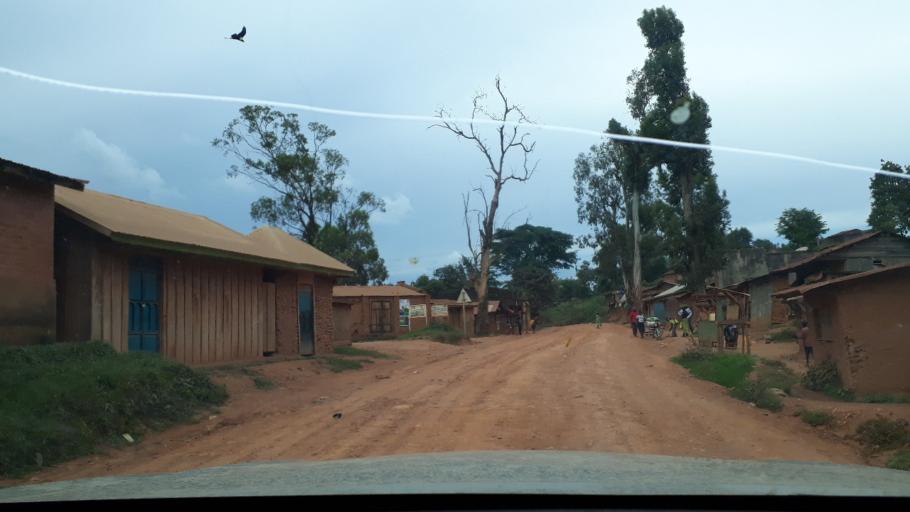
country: CD
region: Eastern Province
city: Bunia
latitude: 1.7872
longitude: 30.3876
